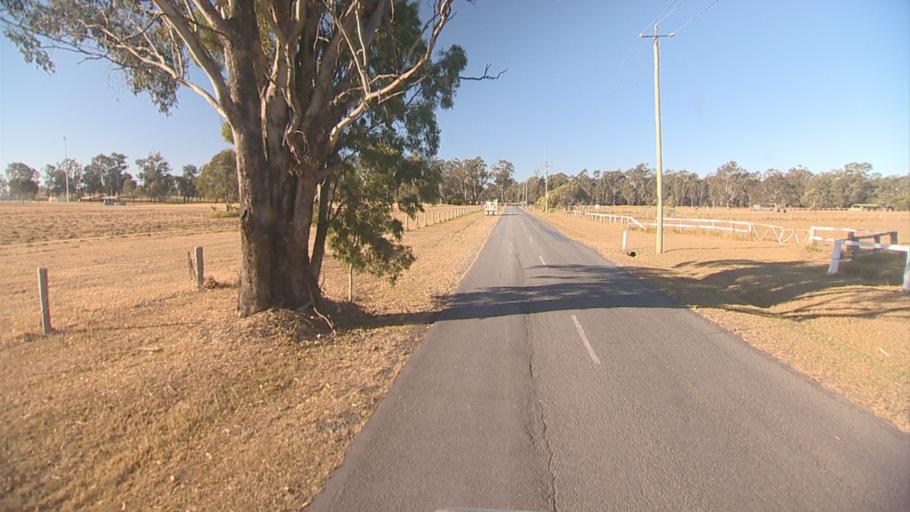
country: AU
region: Queensland
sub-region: Logan
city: Cedar Vale
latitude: -27.8297
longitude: 153.0110
